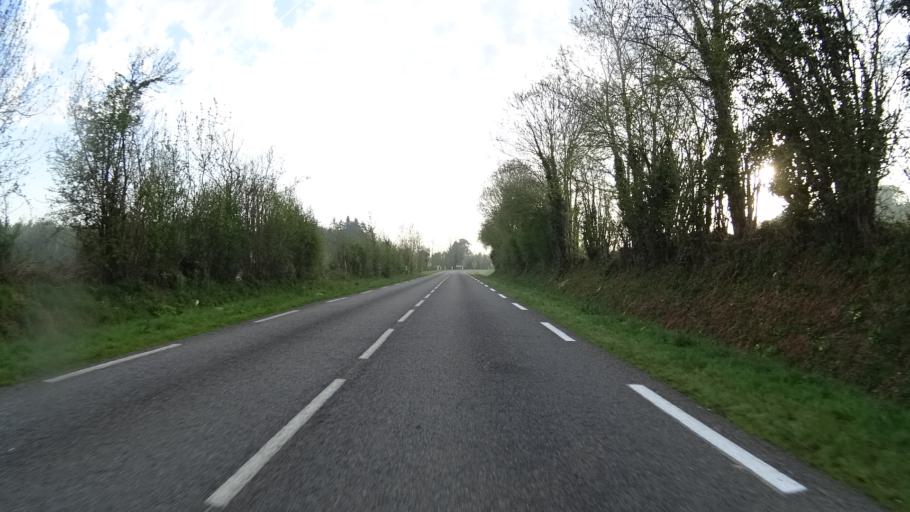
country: FR
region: Brittany
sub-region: Departement du Finistere
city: La Roche-Maurice
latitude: 48.4659
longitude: -4.2123
